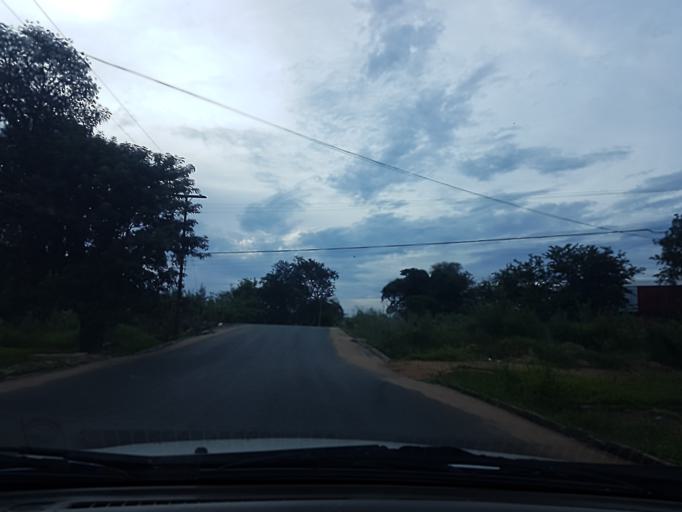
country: PY
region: Central
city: San Lorenzo
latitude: -25.2639
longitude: -57.4784
